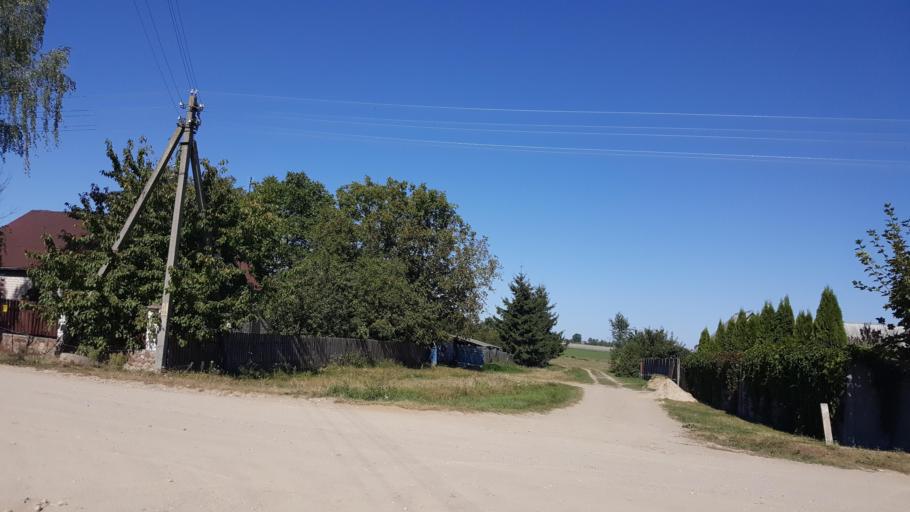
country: BY
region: Brest
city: Vysokaye
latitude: 52.2635
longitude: 23.5003
